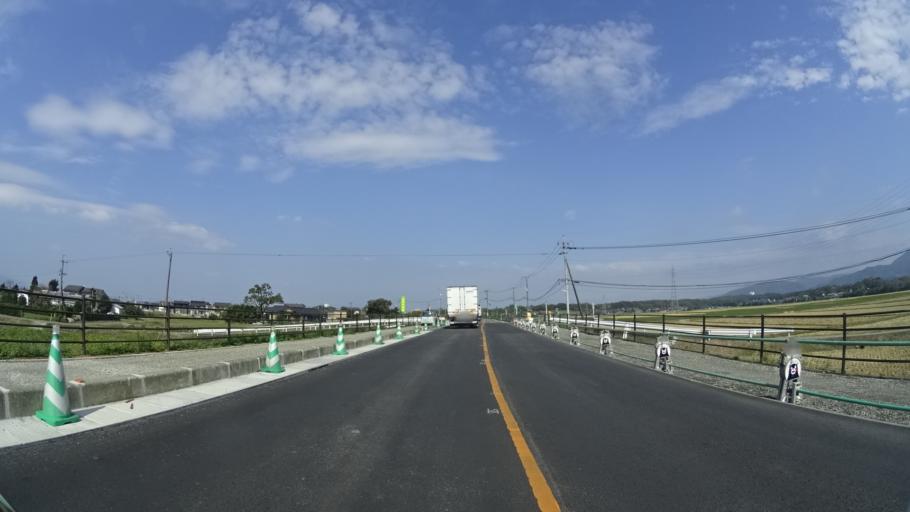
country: JP
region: Kumamoto
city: Kumamoto
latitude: 32.7361
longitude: 130.7718
